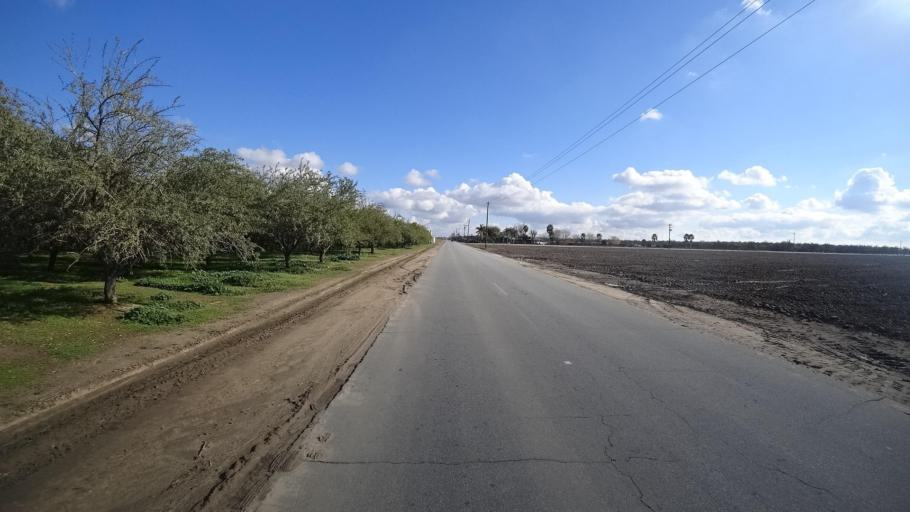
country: US
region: California
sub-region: Kern County
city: McFarland
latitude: 35.6743
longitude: -119.2607
